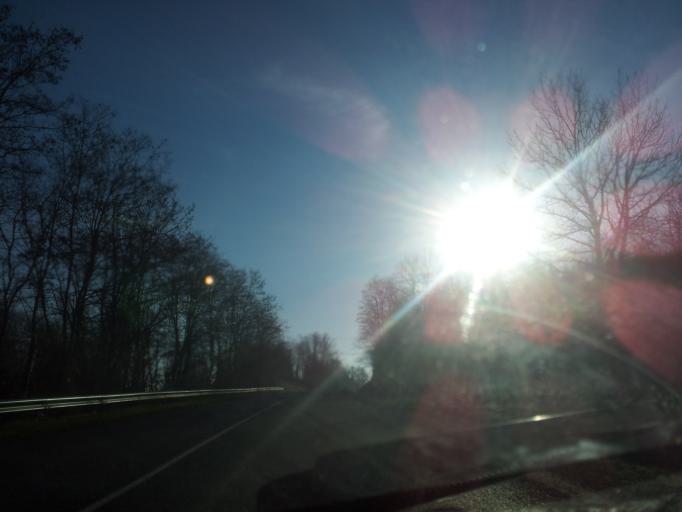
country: FR
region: Auvergne
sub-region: Departement de l'Allier
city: Saint-Pourcain-sur-Sioule
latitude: 46.3173
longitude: 3.2495
